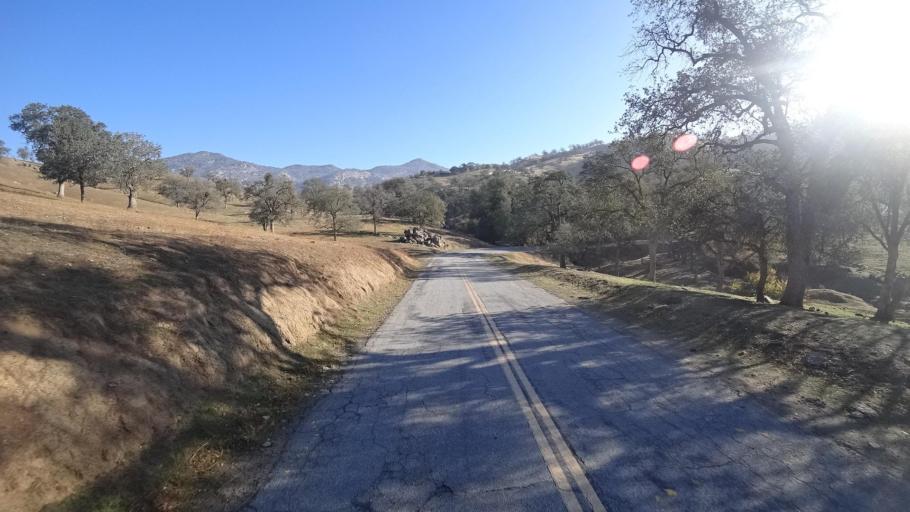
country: US
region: California
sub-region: Kern County
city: Alta Sierra
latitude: 35.7299
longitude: -118.8108
